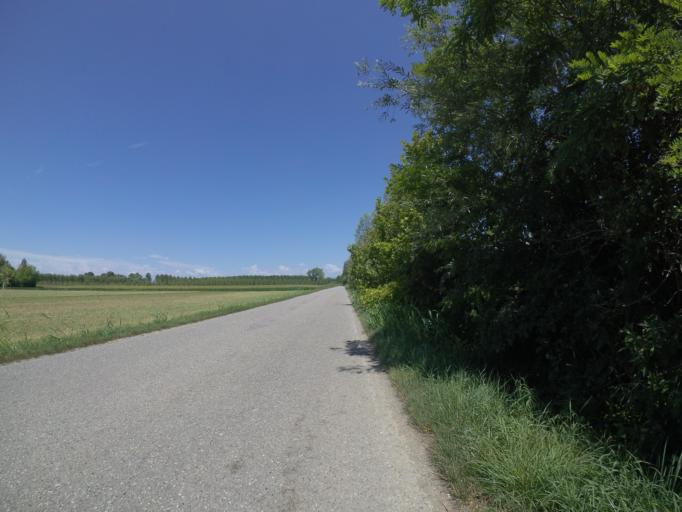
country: IT
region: Friuli Venezia Giulia
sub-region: Provincia di Udine
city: Talmassons
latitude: 45.8933
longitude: 13.1159
